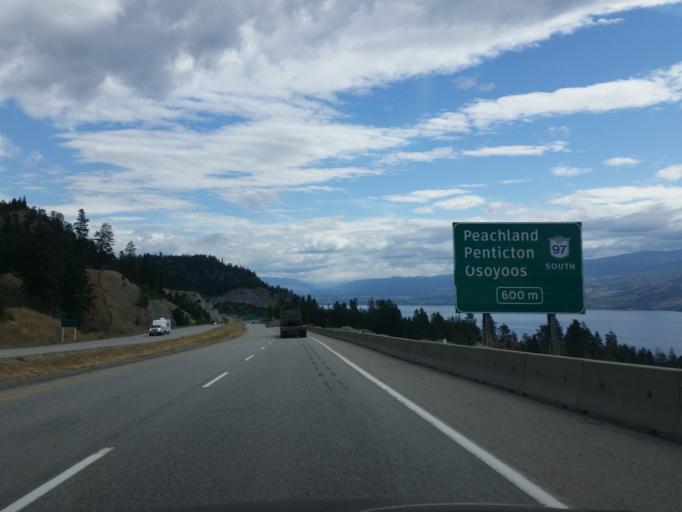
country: CA
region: British Columbia
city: Peachland
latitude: 49.8020
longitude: -119.6803
